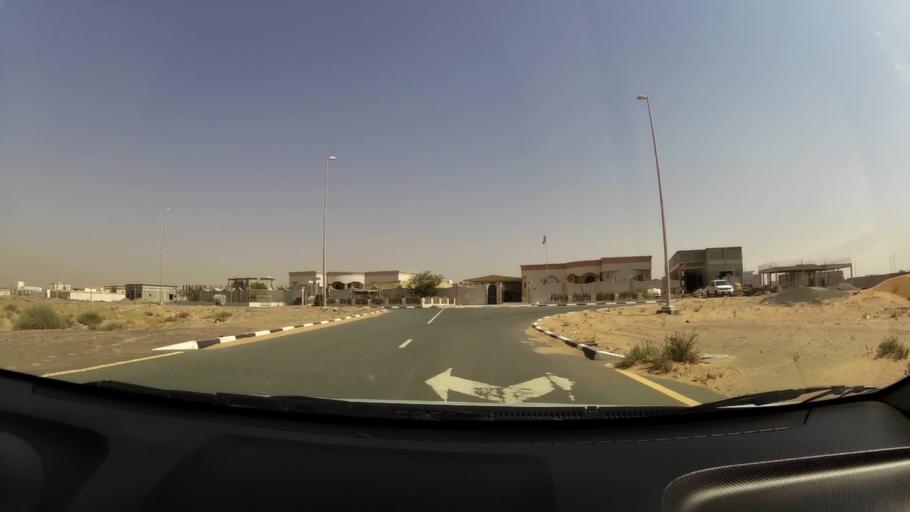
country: AE
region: Umm al Qaywayn
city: Umm al Qaywayn
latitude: 25.4823
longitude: 55.6107
